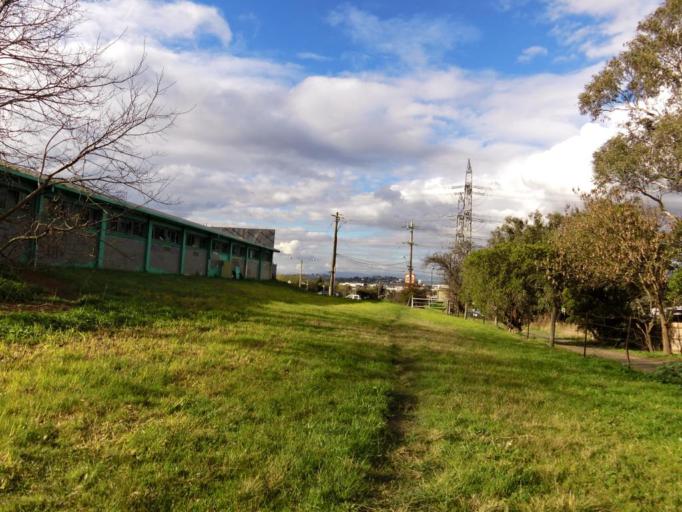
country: AU
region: Victoria
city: Mitcham
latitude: -37.8180
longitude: 145.2126
